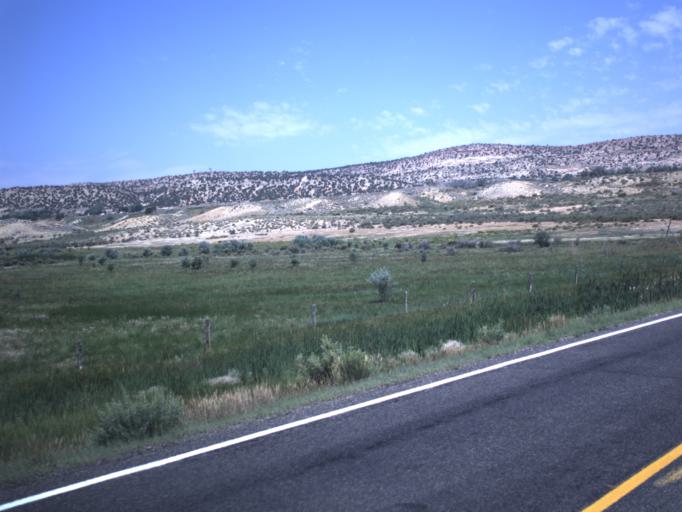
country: US
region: Utah
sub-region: Daggett County
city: Manila
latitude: 40.9766
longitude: -109.7224
